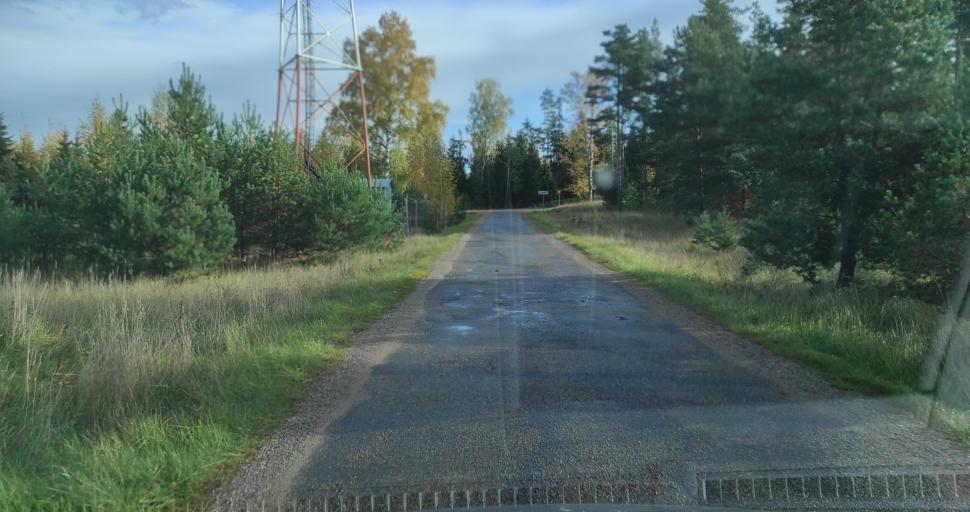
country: LV
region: Skrunda
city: Skrunda
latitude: 56.6845
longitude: 22.0577
